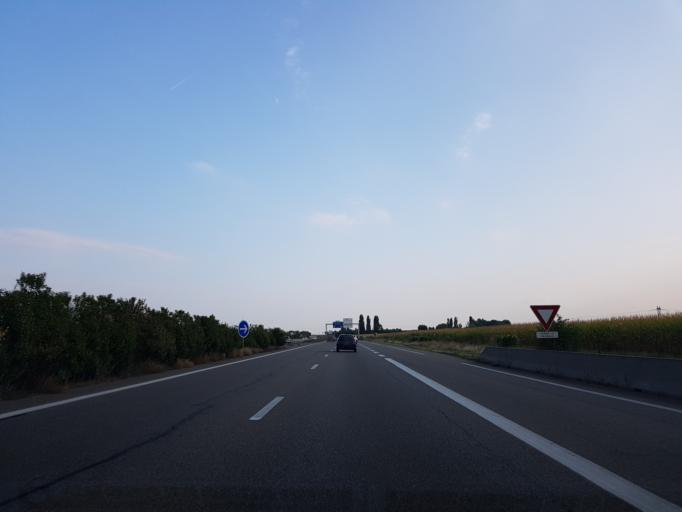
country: FR
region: Alsace
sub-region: Departement du Haut-Rhin
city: Sainte-Croix-en-Plaine
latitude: 48.0244
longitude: 7.3725
